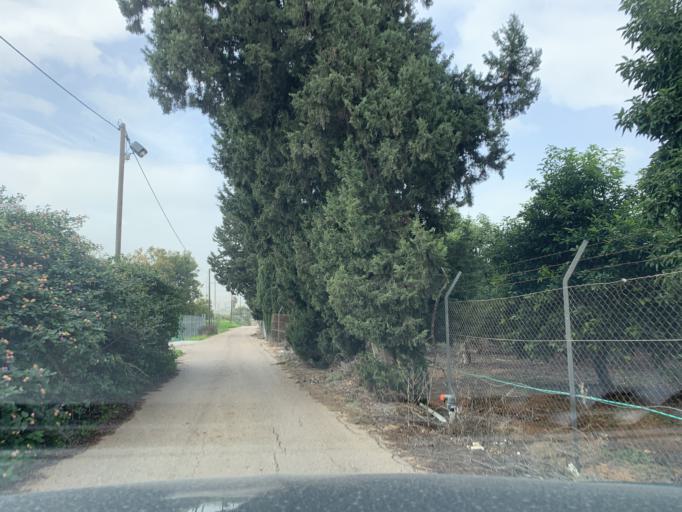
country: IL
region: Central District
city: Jaljulya
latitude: 32.1628
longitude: 34.9452
